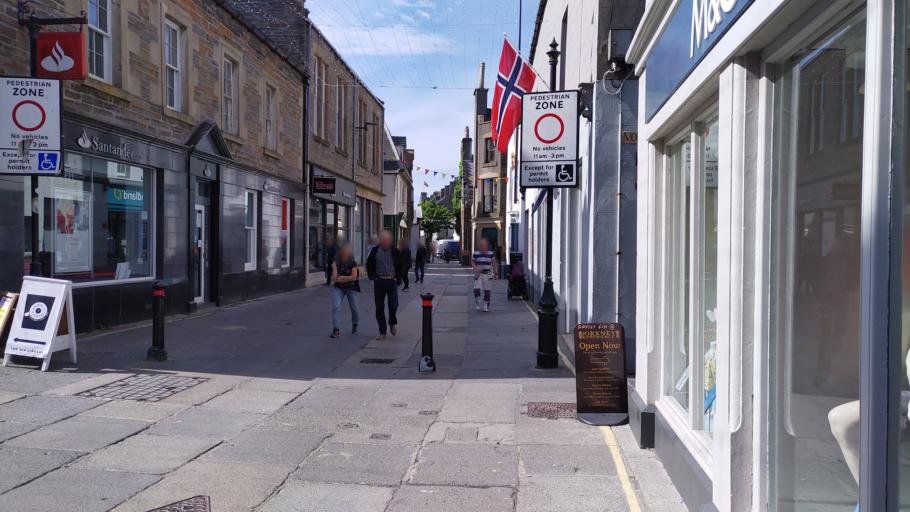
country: GB
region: Scotland
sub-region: Orkney Islands
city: Kirkwall
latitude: 58.9834
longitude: -2.9583
